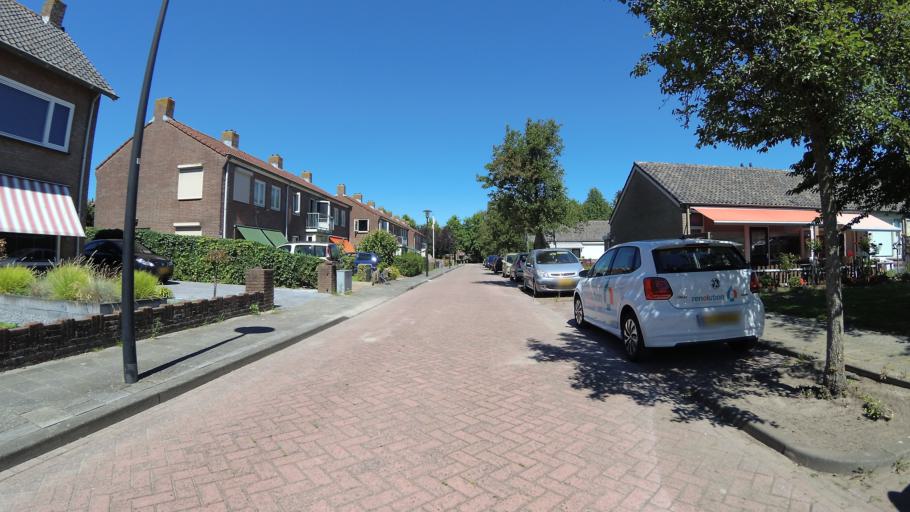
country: NL
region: North Brabant
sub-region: Gemeente Waalwijk
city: Waalwijk
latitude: 51.6711
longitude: 5.0457
